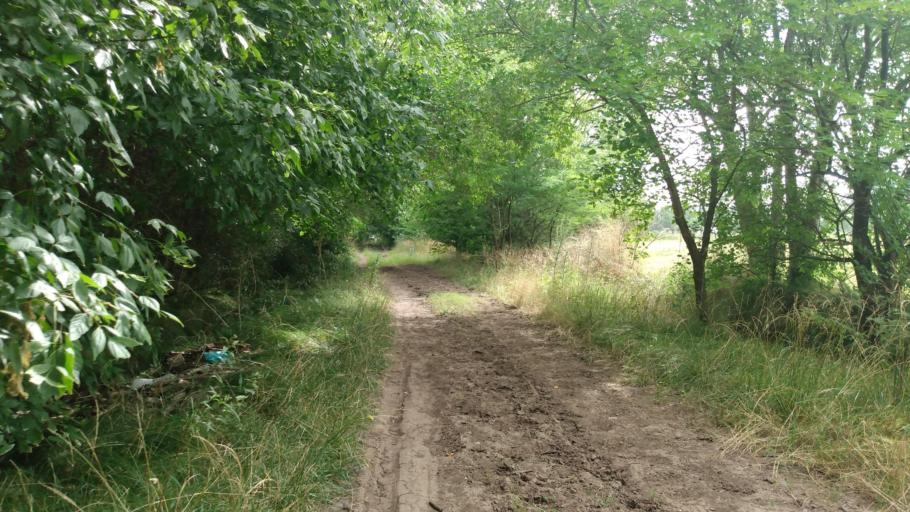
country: AR
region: Buenos Aires
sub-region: Partido de Lujan
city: Lujan
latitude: -34.5996
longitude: -59.0616
